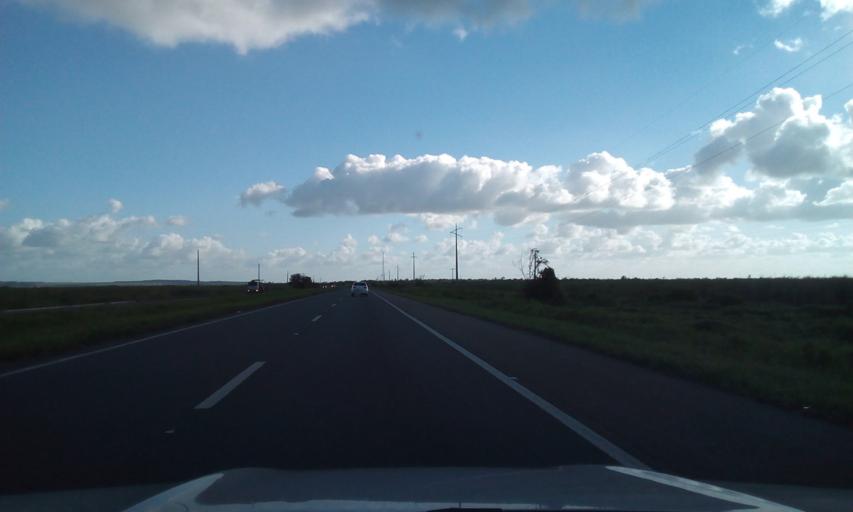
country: BR
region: Paraiba
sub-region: Cruz Do Espirito Santo
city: Cruz do Espirito Santo
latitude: -7.1900
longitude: -35.0620
